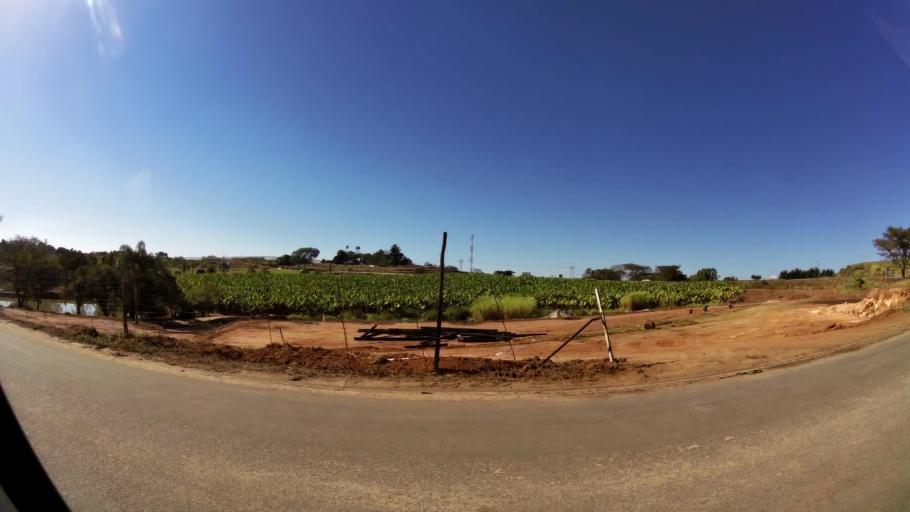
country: ZA
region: Limpopo
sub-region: Mopani District Municipality
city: Tzaneen
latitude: -23.8353
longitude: 30.1331
